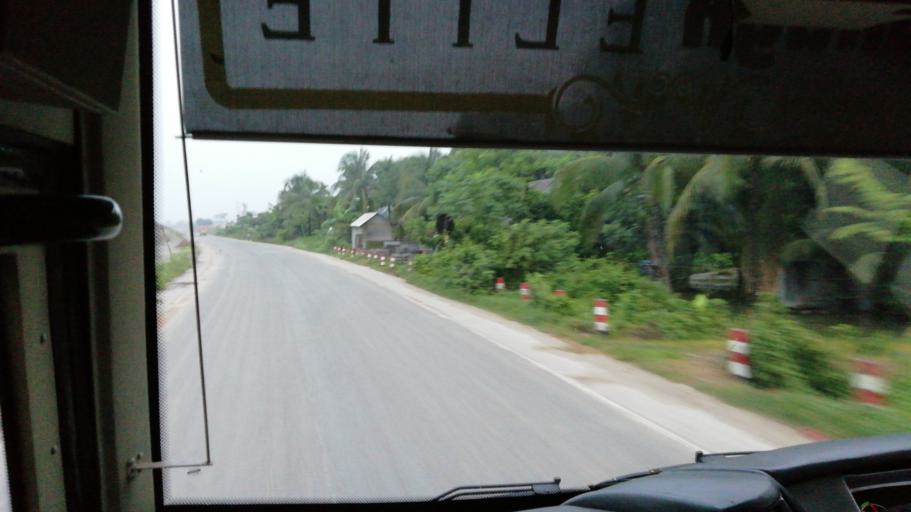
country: BD
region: Dhaka
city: Char Bhadrasan
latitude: 23.4035
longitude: 90.1490
